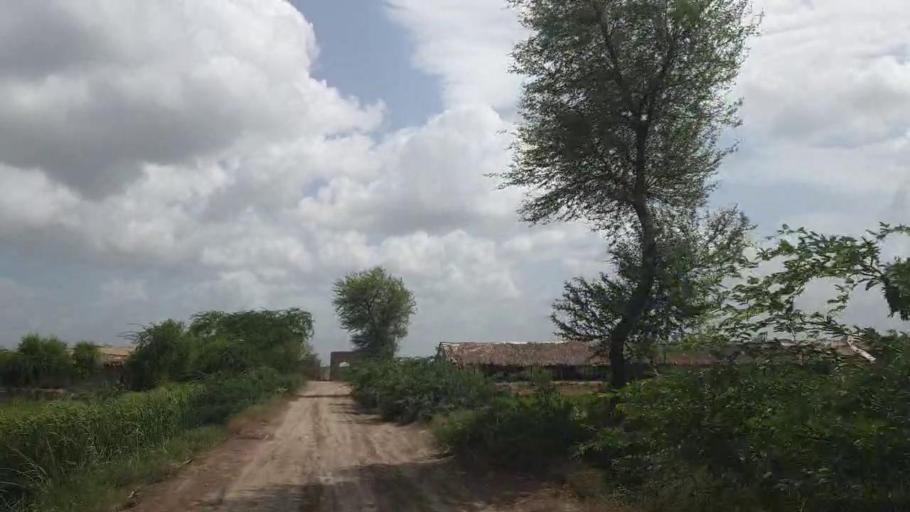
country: PK
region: Sindh
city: Tando Bago
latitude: 24.6501
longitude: 68.9979
